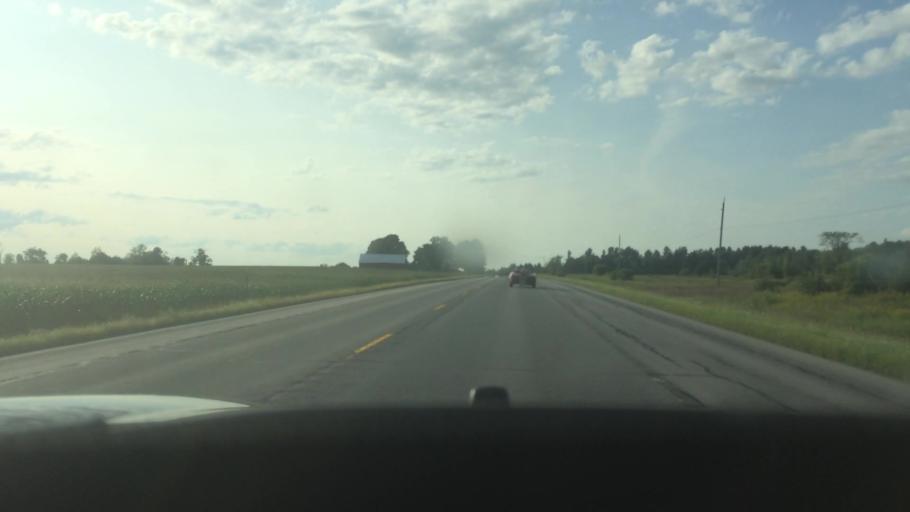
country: US
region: New York
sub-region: St. Lawrence County
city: Canton
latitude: 44.6257
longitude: -75.2360
